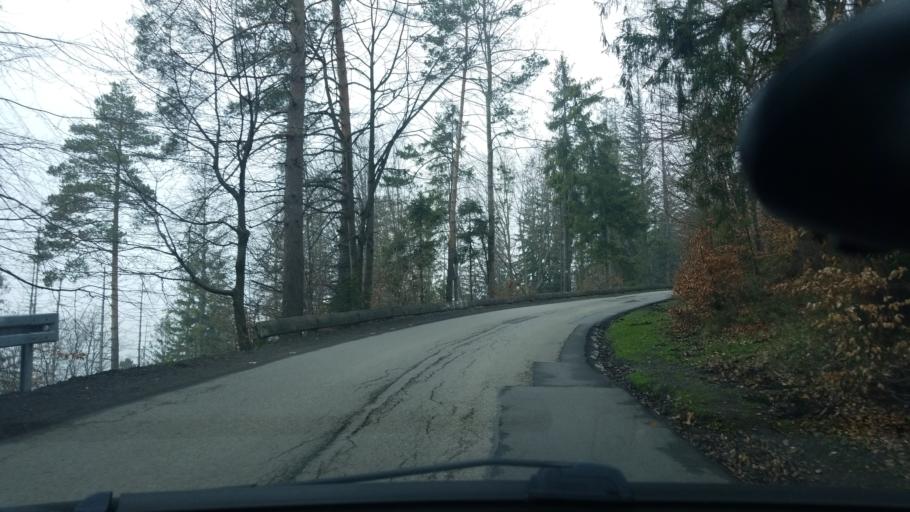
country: PL
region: Silesian Voivodeship
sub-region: Powiat cieszynski
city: Ustron
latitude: 49.7160
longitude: 18.8424
